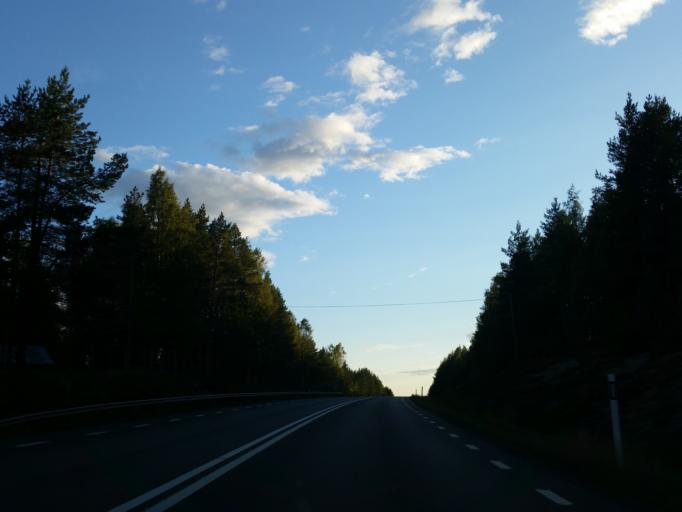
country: SE
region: Vaesterbotten
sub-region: Robertsfors Kommun
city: Robertsfors
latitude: 64.0171
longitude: 20.8313
